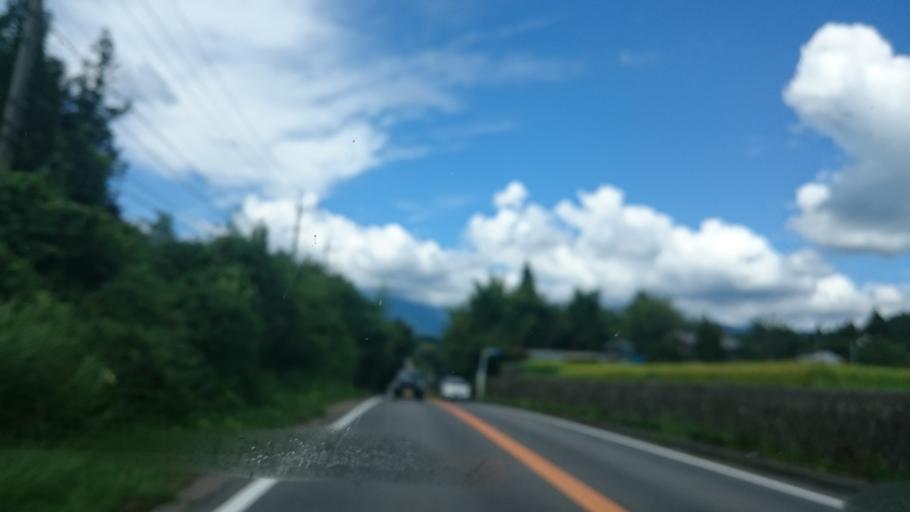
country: JP
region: Gifu
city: Nakatsugawa
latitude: 35.5658
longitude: 137.4531
